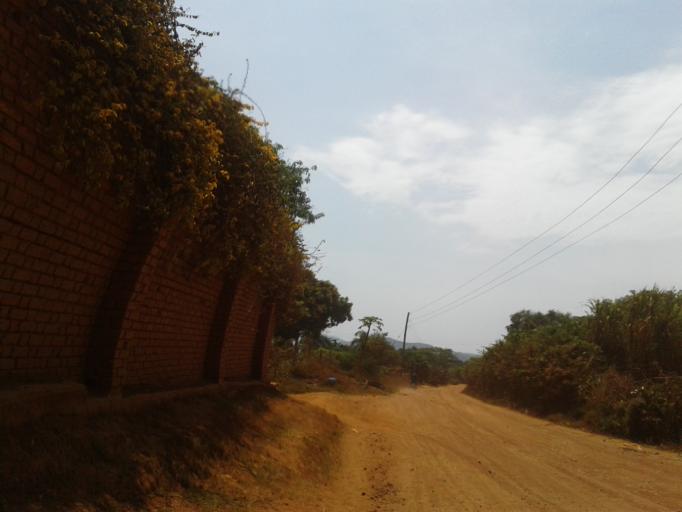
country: UG
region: Central Region
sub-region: Kampala District
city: Kampala
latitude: 0.2639
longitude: 32.6309
